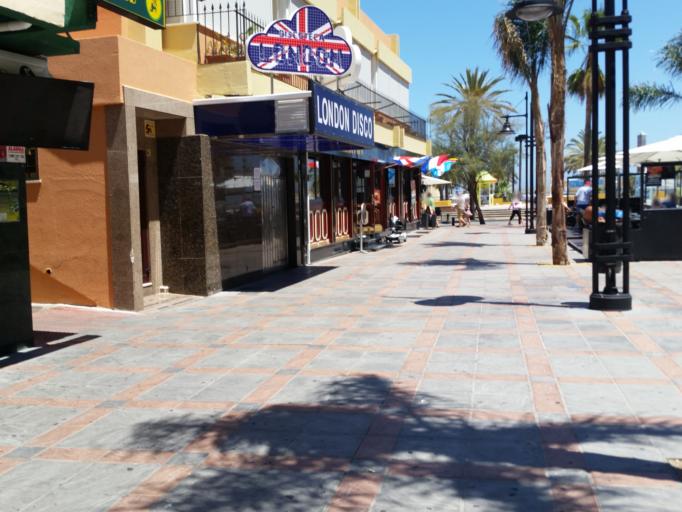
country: ES
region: Andalusia
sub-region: Provincia de Malaga
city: Fuengirola
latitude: 36.5422
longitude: -4.6198
